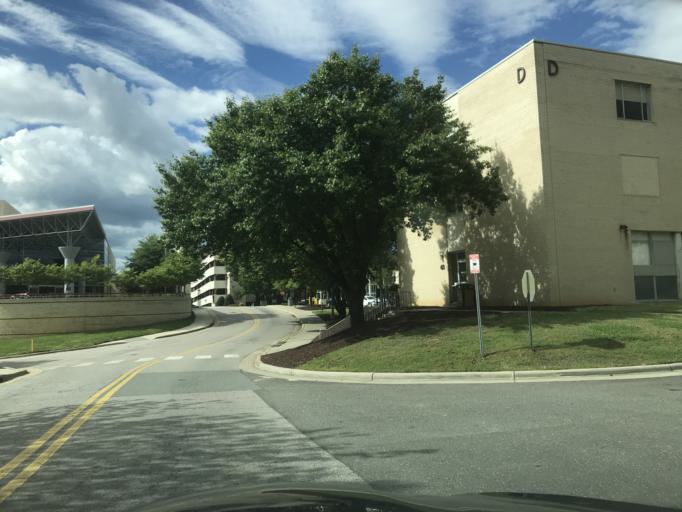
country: US
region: North Carolina
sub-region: Wake County
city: Raleigh
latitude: 35.7840
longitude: -78.5862
